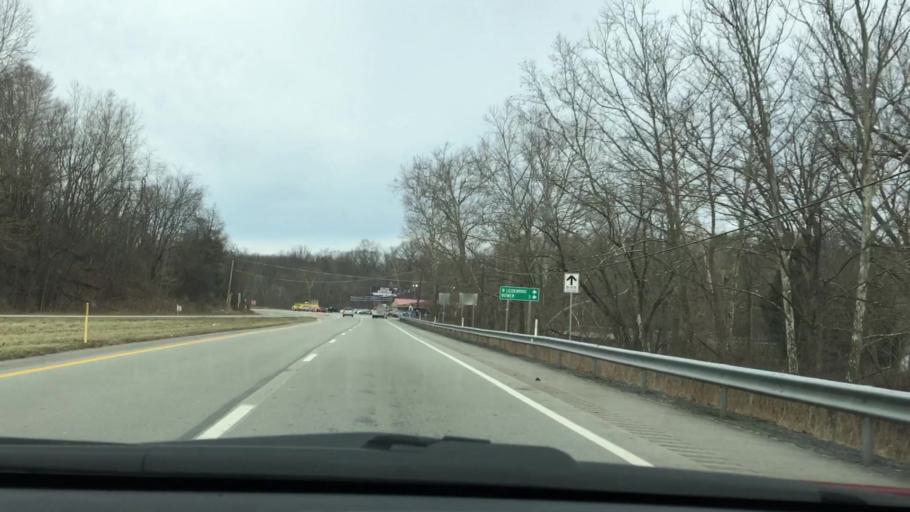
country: US
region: Pennsylvania
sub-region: Fayette County
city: Oliver
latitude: 39.9498
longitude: -79.7347
